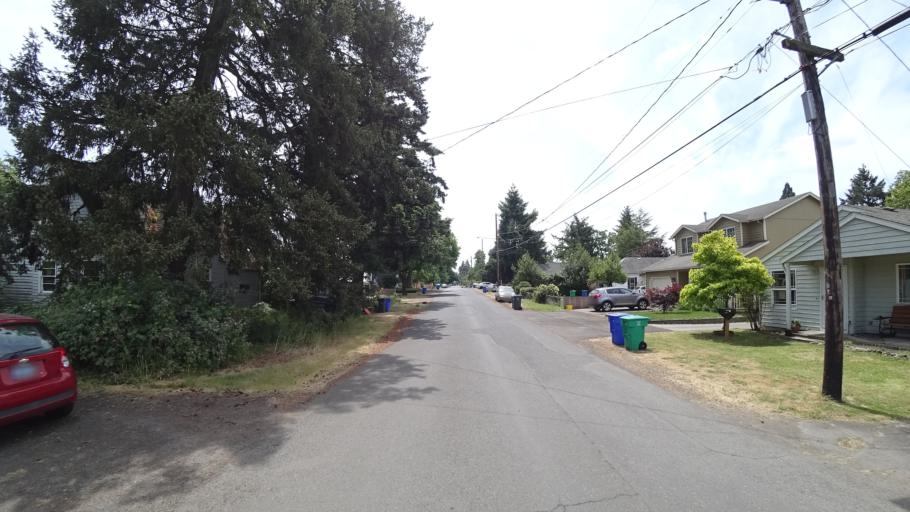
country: US
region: Oregon
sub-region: Multnomah County
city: Lents
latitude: 45.4750
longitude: -122.5932
